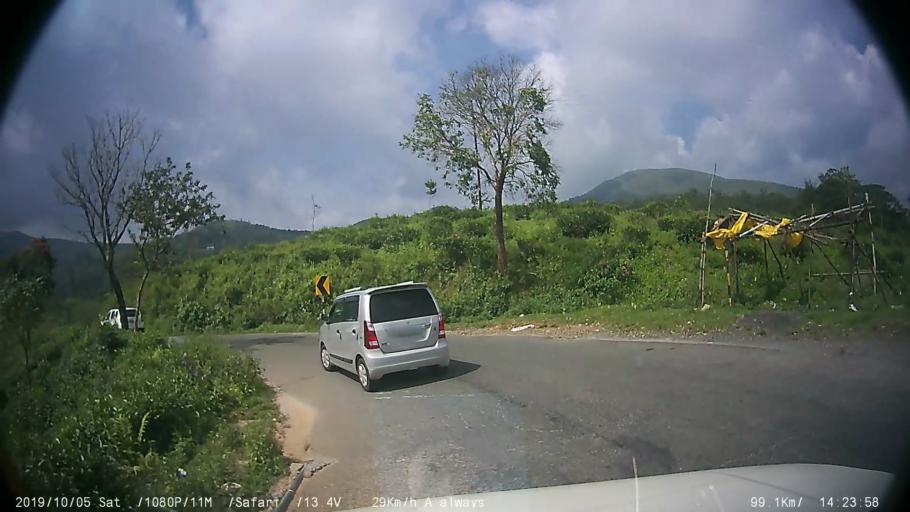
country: IN
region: Kerala
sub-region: Kottayam
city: Erattupetta
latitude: 9.5928
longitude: 76.9692
